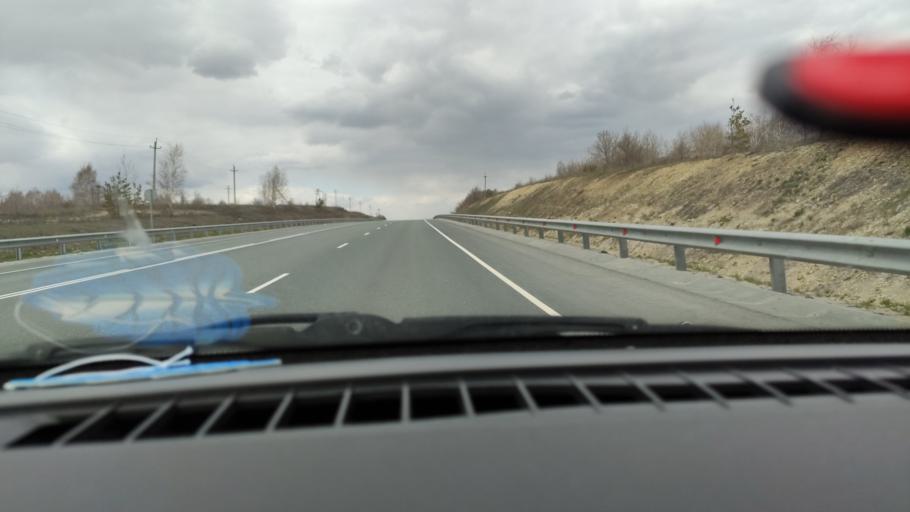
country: RU
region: Saratov
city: Shikhany
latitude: 52.1459
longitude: 47.1982
